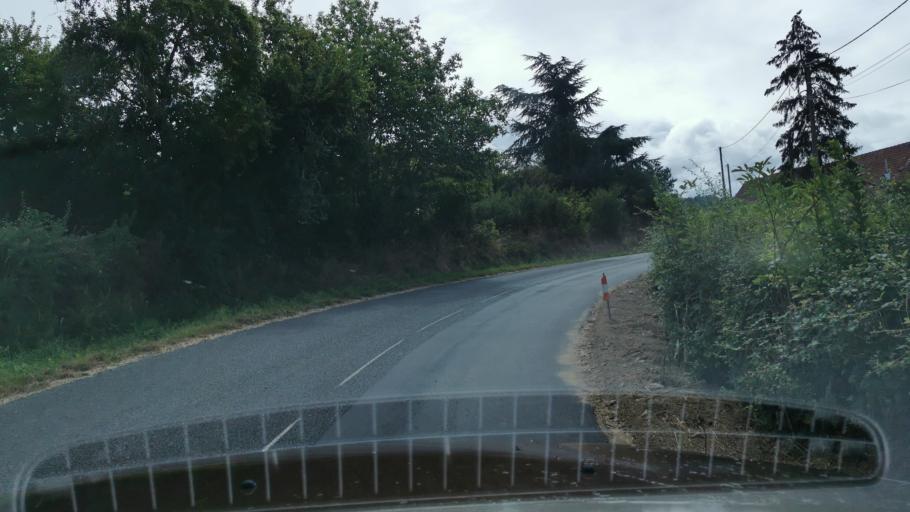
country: FR
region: Bourgogne
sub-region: Departement de Saone-et-Loire
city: Marmagne
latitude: 46.8049
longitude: 4.3383
